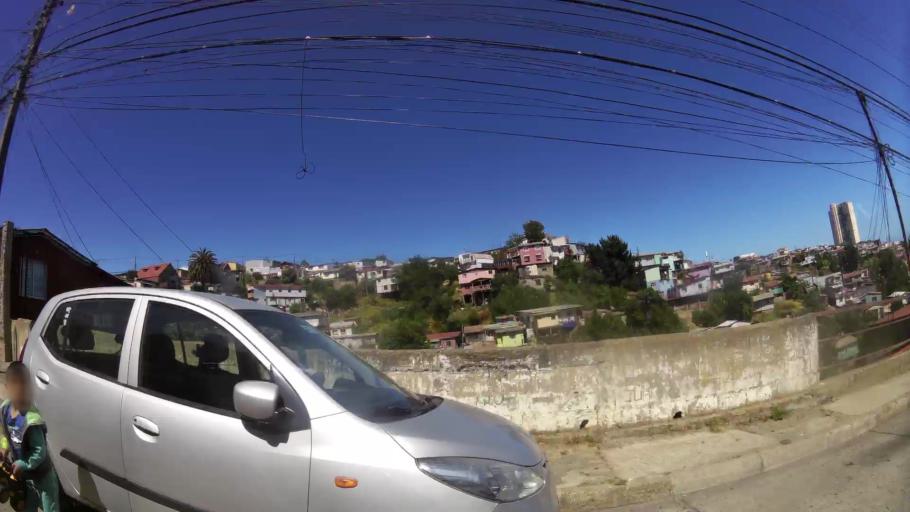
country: CL
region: Valparaiso
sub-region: Provincia de Valparaiso
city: Valparaiso
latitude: -33.0478
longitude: -71.5898
